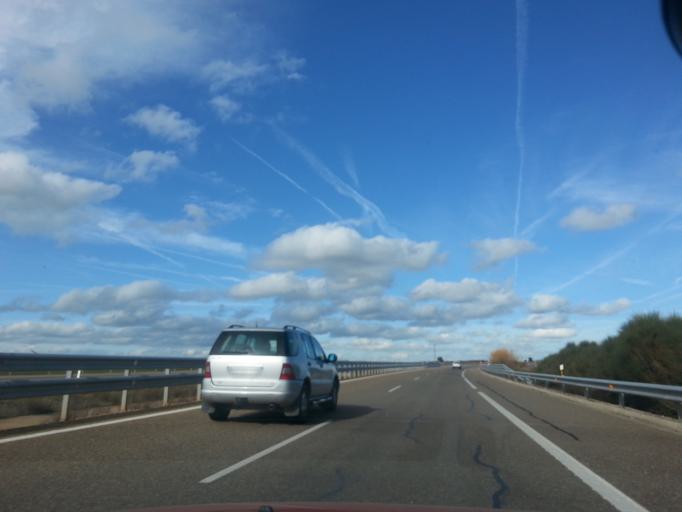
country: ES
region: Castille and Leon
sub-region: Provincia de Salamanca
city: Galindo y Perahuy
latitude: 40.9128
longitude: -5.8638
